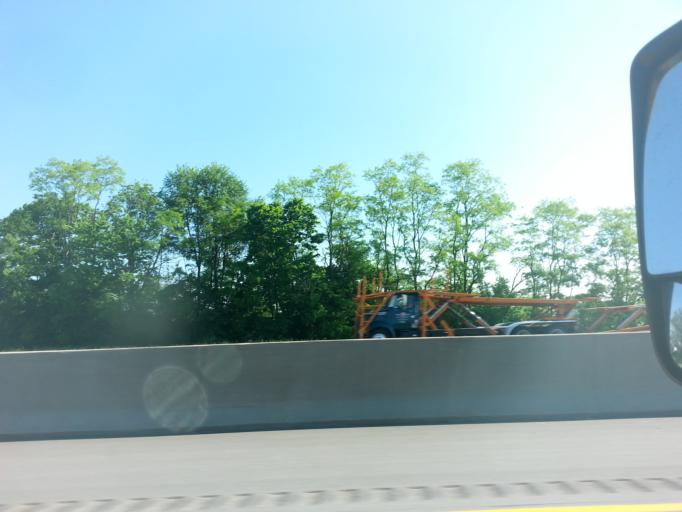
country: US
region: Kentucky
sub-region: Shelby County
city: Shelbyville
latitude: 38.1947
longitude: -85.2804
